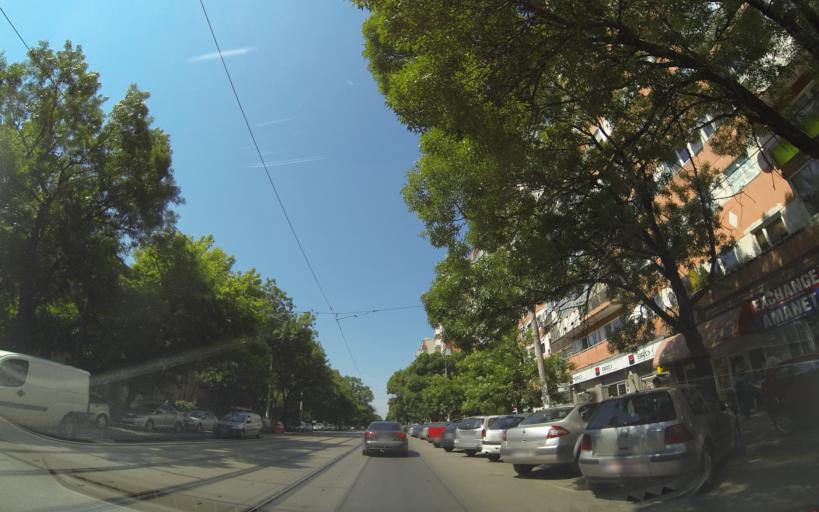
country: RO
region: Bucuresti
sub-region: Municipiul Bucuresti
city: Bucuresti
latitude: 44.4048
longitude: 26.0610
